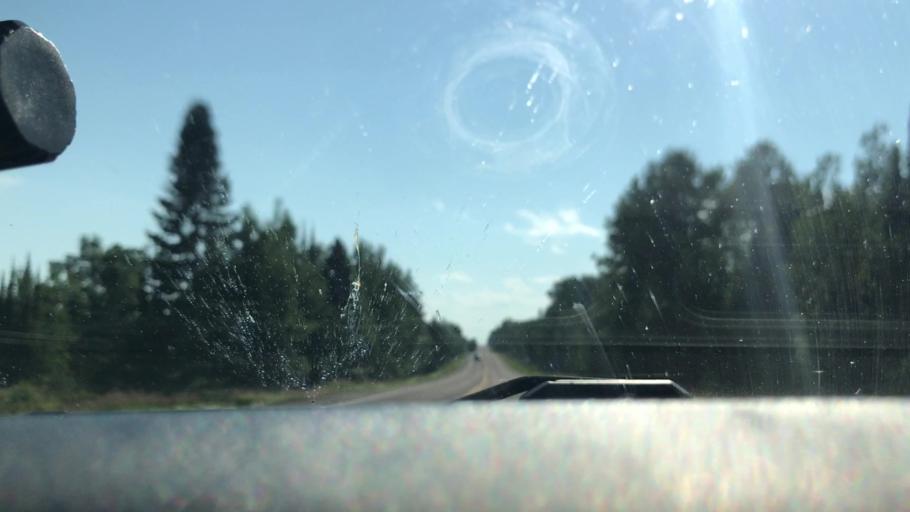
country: US
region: Minnesota
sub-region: Cook County
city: Grand Marais
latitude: 47.8270
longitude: -90.0115
